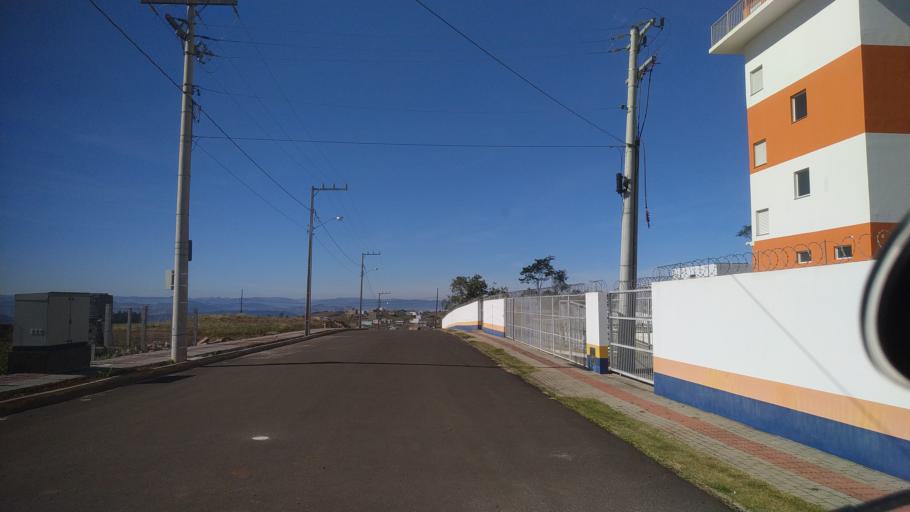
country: BR
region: Santa Catarina
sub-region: Chapeco
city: Chapeco
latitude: -27.0486
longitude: -52.6039
